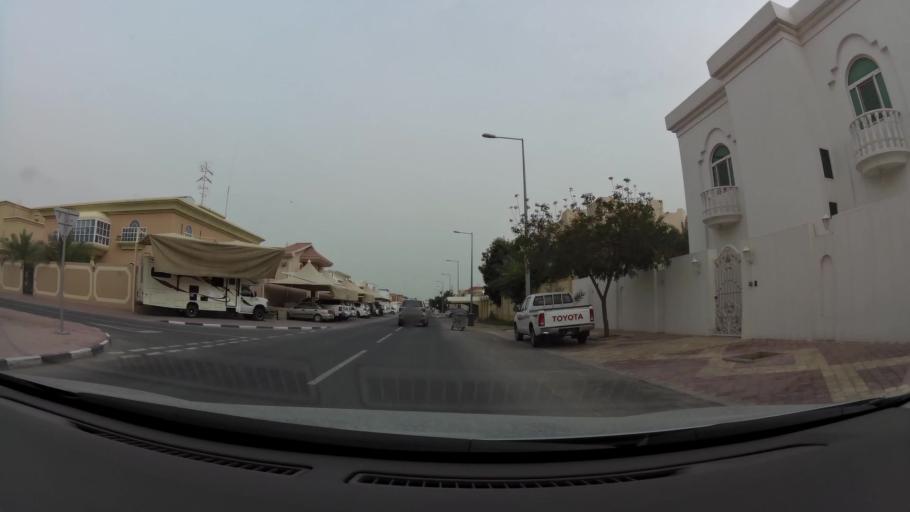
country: QA
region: Baladiyat ad Dawhah
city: Doha
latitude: 25.2482
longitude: 51.5078
